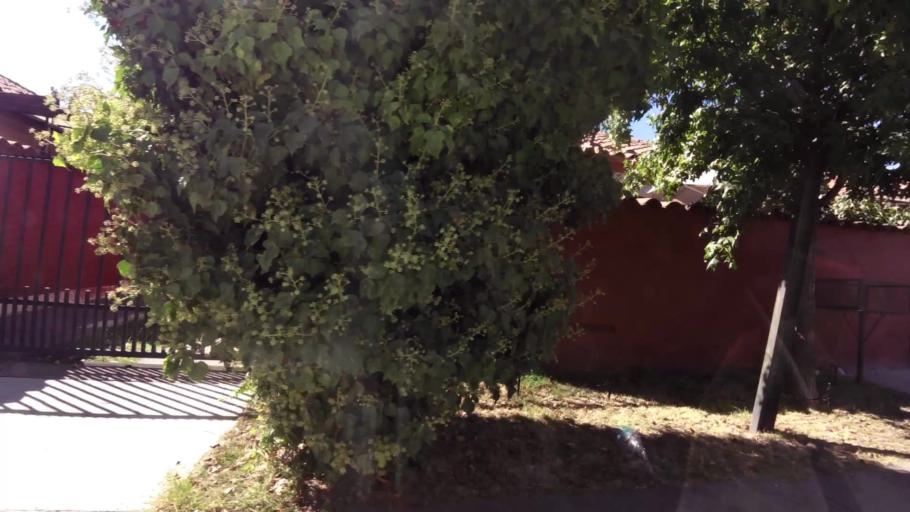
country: CL
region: O'Higgins
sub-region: Provincia de Cachapoal
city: Rancagua
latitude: -34.1795
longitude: -70.7046
